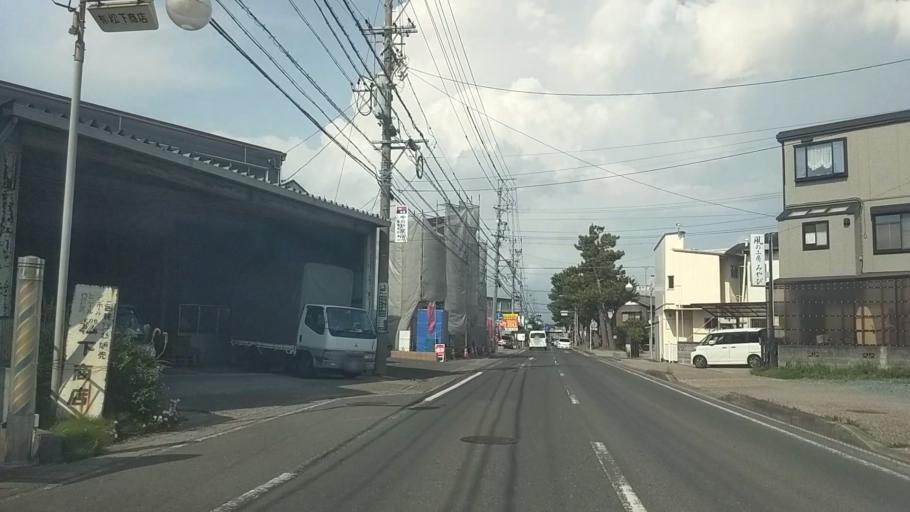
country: JP
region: Shizuoka
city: Hamamatsu
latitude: 34.7231
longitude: 137.7827
